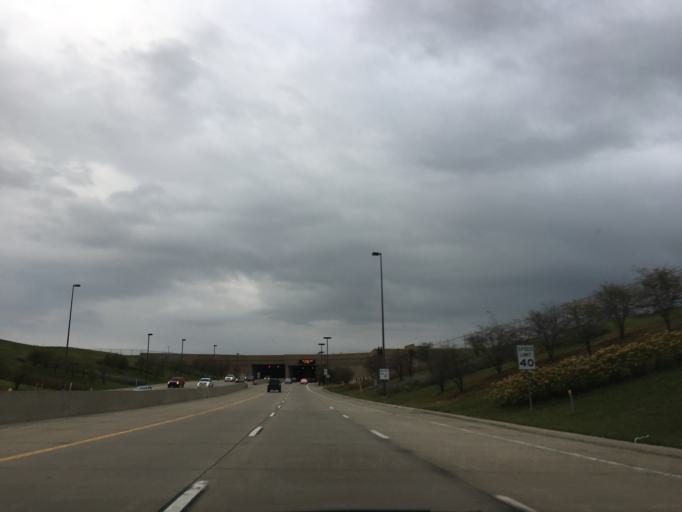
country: US
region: Missouri
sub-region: Saint Louis County
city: Bridgeton
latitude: 38.7502
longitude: -90.3947
